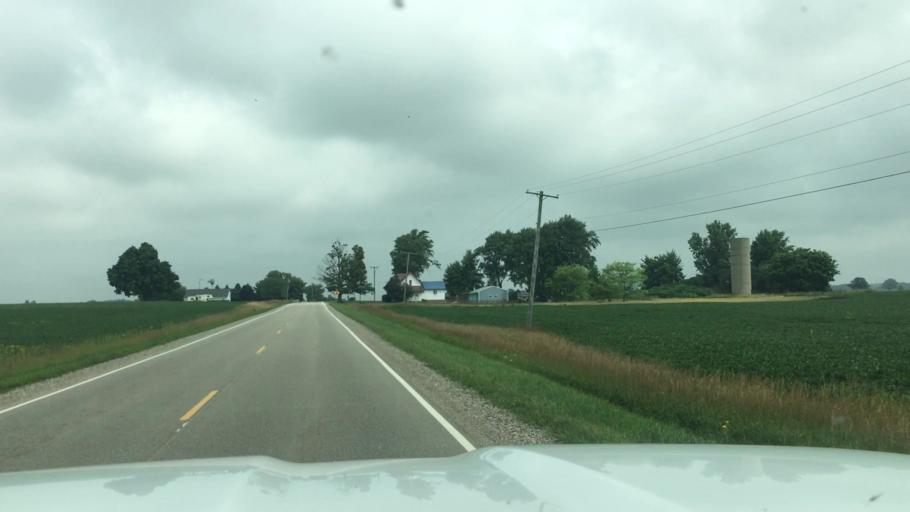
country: US
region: Michigan
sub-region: Sanilac County
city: Marlette
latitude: 43.3256
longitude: -82.9842
